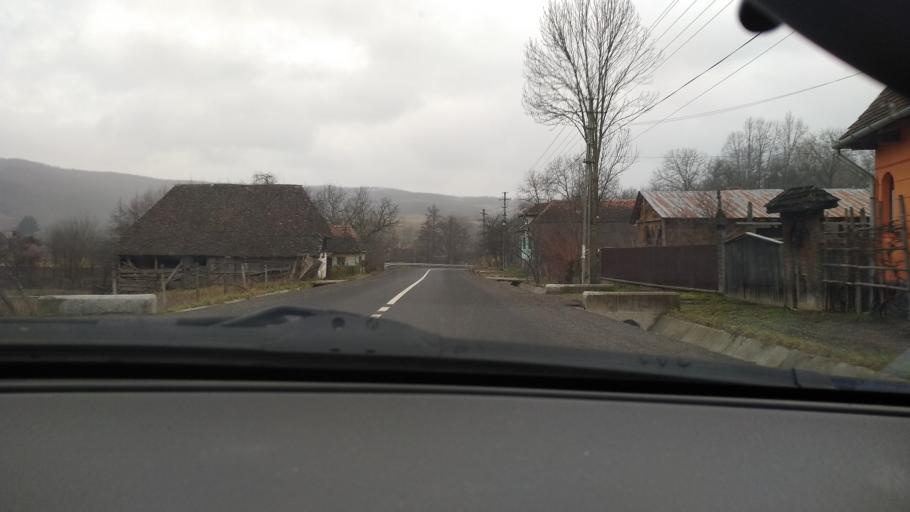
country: RO
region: Mures
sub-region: Comuna Magherani
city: Magherani
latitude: 46.5653
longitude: 24.9176
